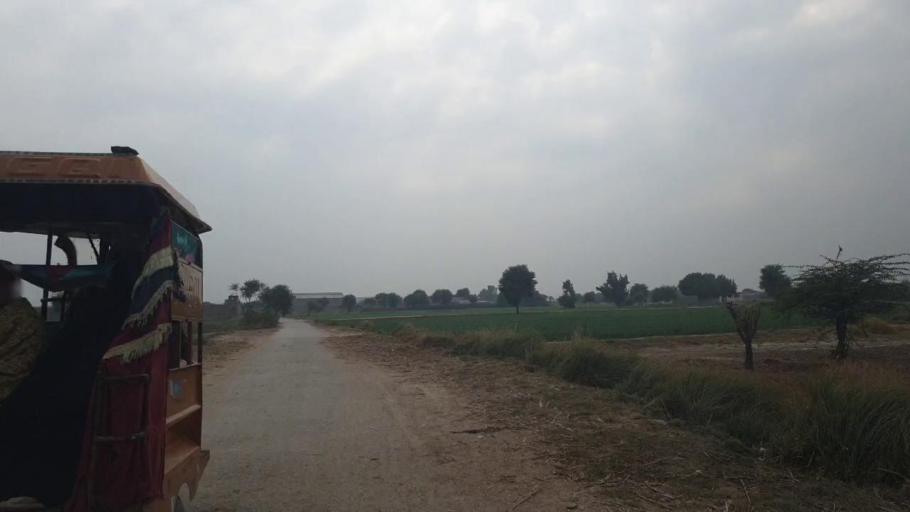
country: PK
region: Sindh
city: Shahdadpur
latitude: 25.9390
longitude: 68.7014
